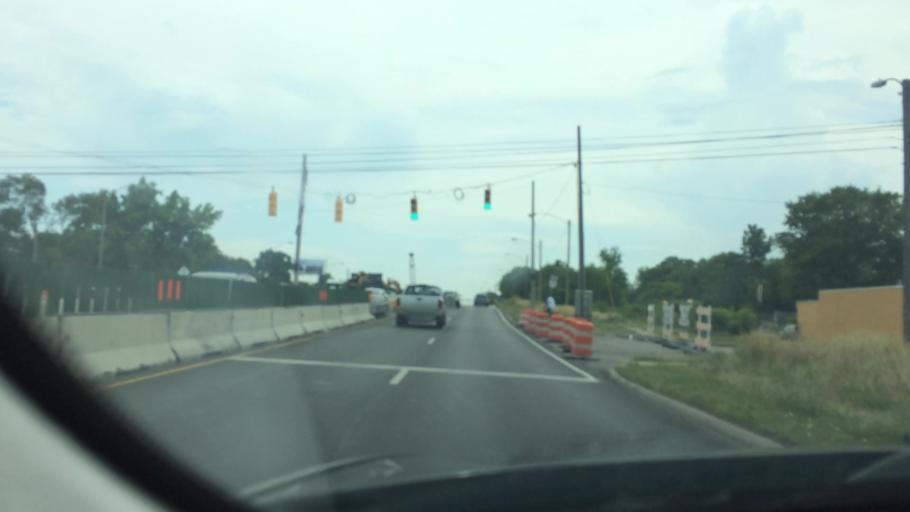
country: US
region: Ohio
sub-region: Lucas County
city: Toledo
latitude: 41.6391
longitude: -83.5552
